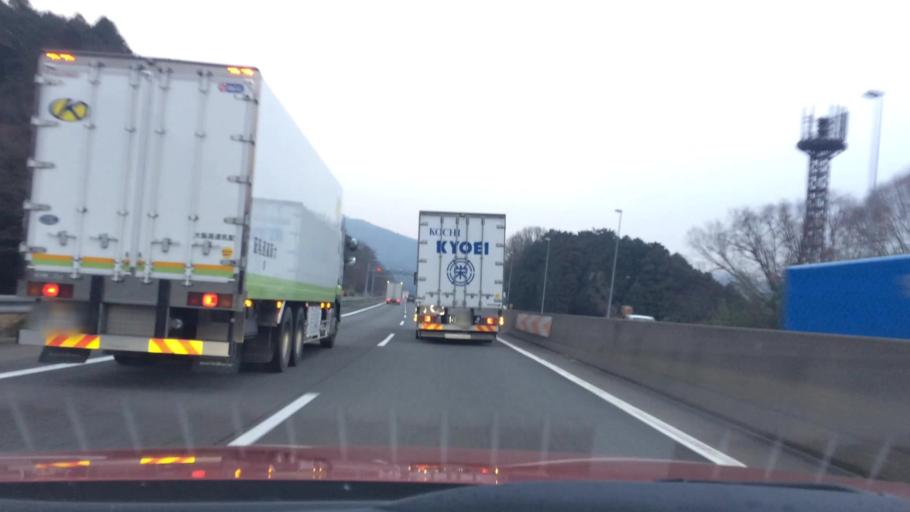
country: JP
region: Gifu
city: Tarui
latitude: 35.3439
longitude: 136.4097
